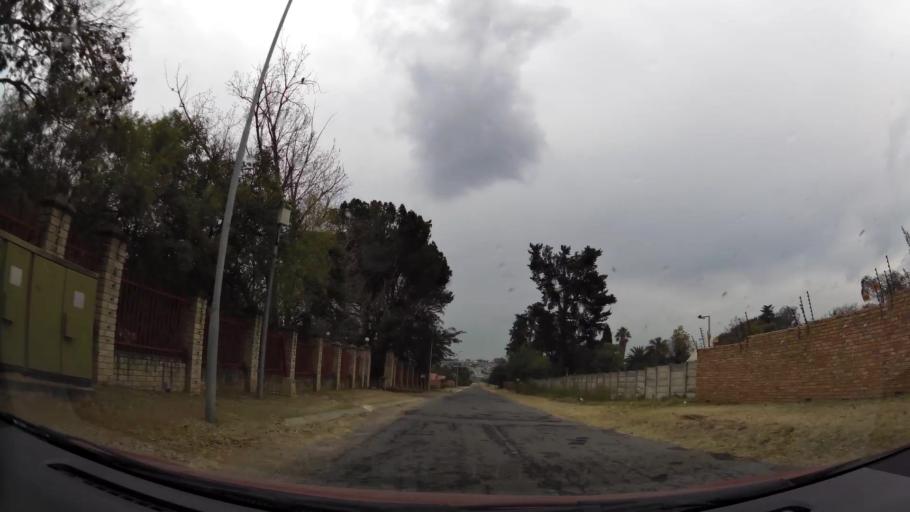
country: ZA
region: Gauteng
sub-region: City of Johannesburg Metropolitan Municipality
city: Roodepoort
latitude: -26.0934
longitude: 27.9133
